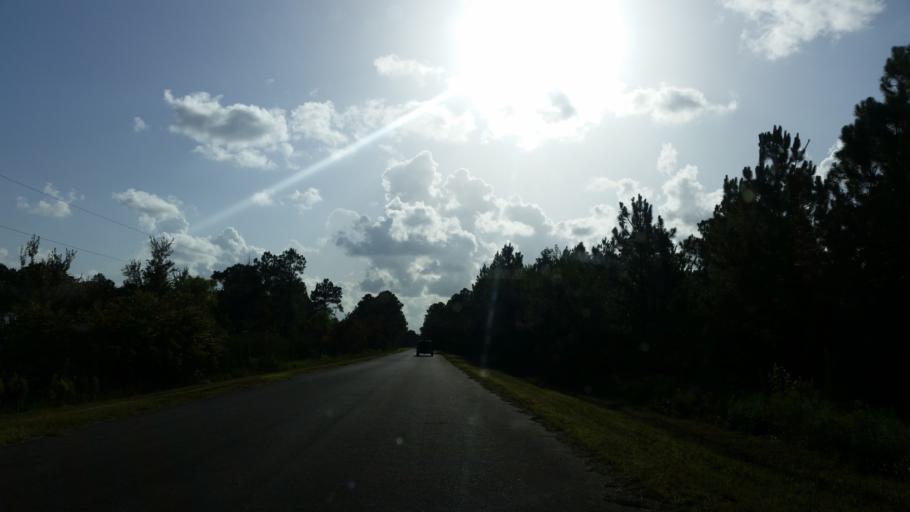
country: US
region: Florida
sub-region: Santa Rosa County
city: Pace
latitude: 30.5346
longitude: -87.1073
